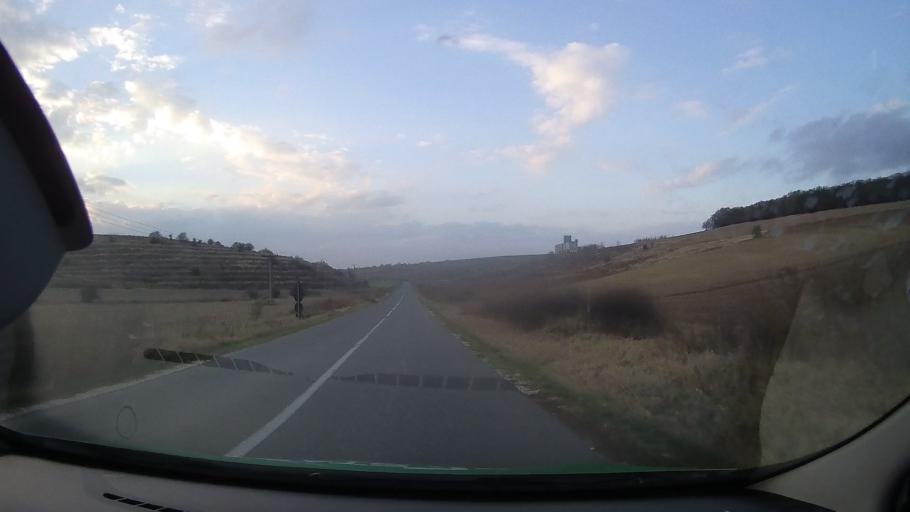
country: RO
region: Constanta
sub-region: Comuna Baneasa
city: Baneasa
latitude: 44.0559
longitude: 27.7229
